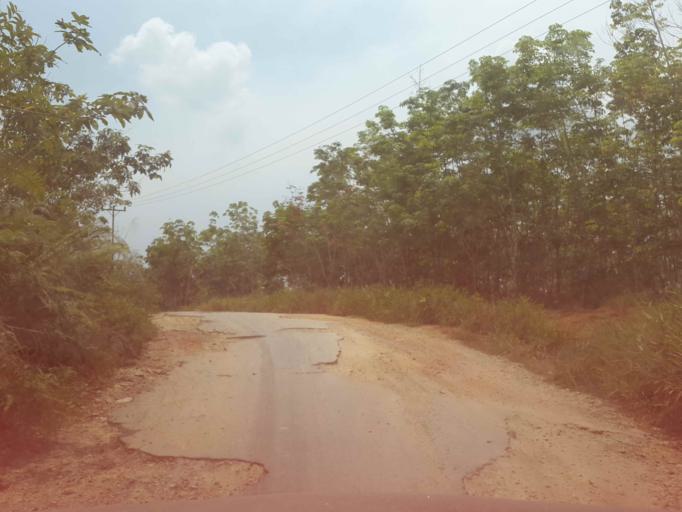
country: MY
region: Sarawak
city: Simanggang
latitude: 1.0079
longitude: 111.8848
